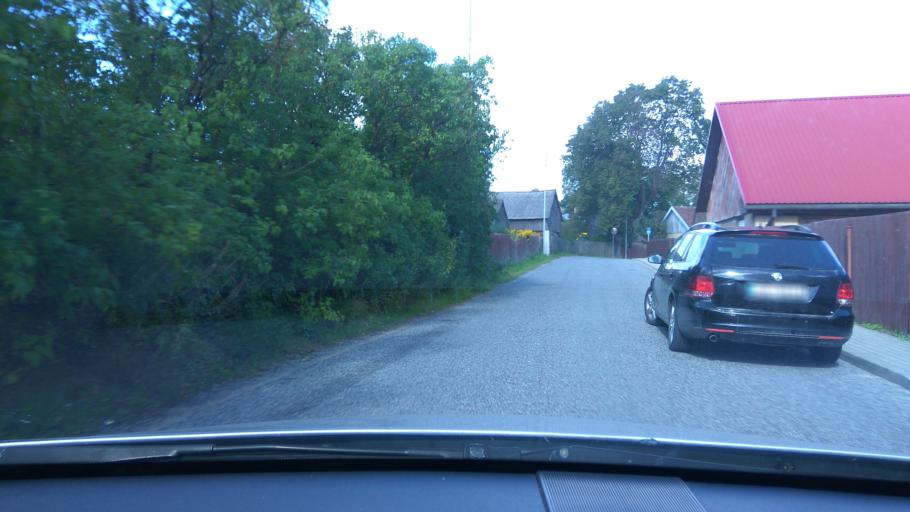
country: LV
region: Kuldigas Rajons
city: Kuldiga
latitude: 56.9689
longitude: 21.9514
